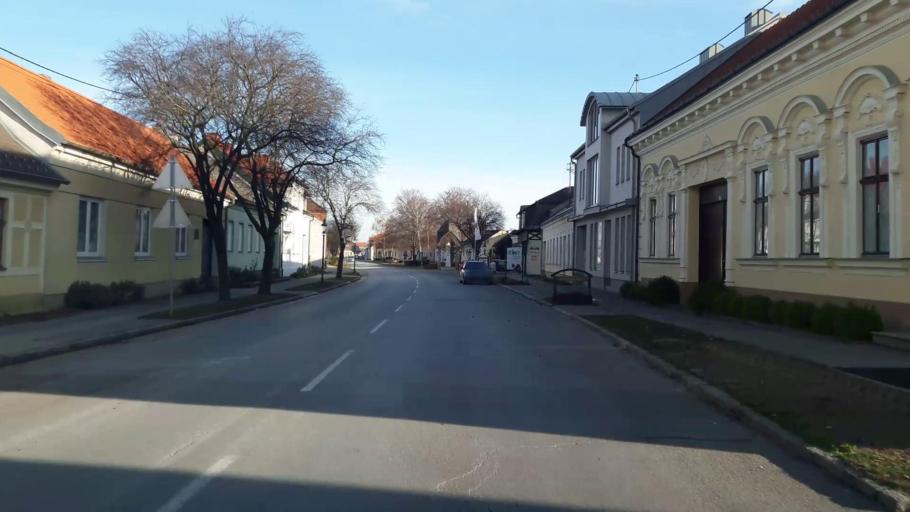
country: AT
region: Lower Austria
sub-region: Politischer Bezirk Mistelbach
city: Bockfliess
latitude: 48.3597
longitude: 16.6045
